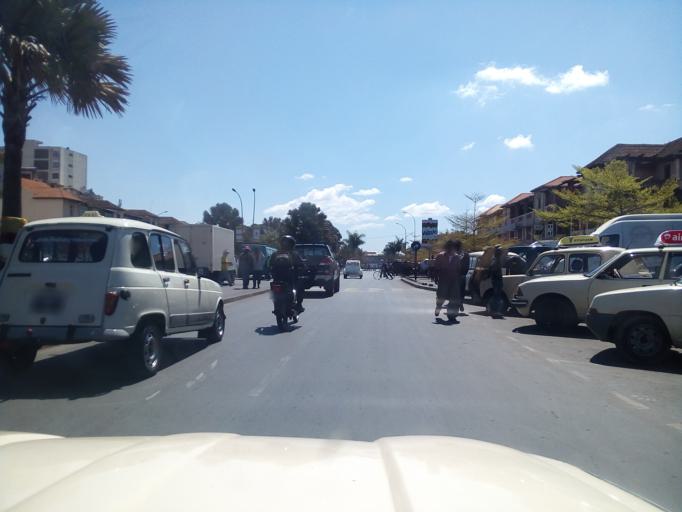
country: MG
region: Analamanga
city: Antananarivo
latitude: -18.9067
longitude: 47.5245
